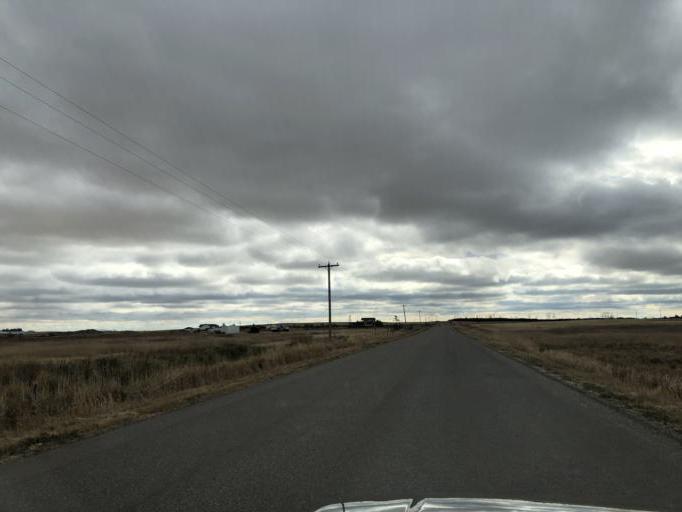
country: CA
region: Alberta
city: Chestermere
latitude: 50.9209
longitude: -113.8830
